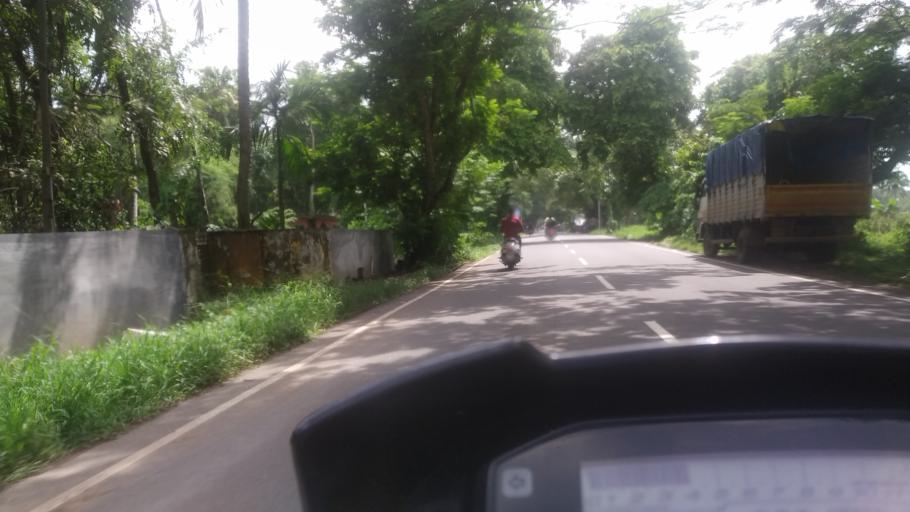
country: IN
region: Kerala
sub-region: Ernakulam
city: Elur
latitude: 10.1306
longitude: 76.2891
